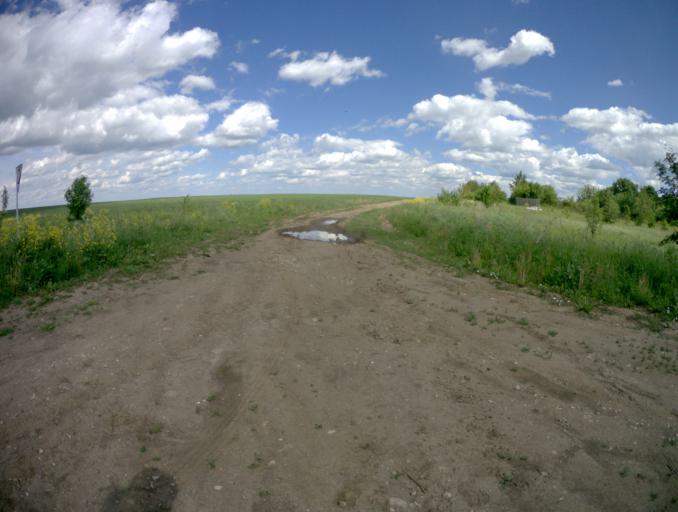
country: RU
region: Vladimir
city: Suzdal'
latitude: 56.4343
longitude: 40.3152
